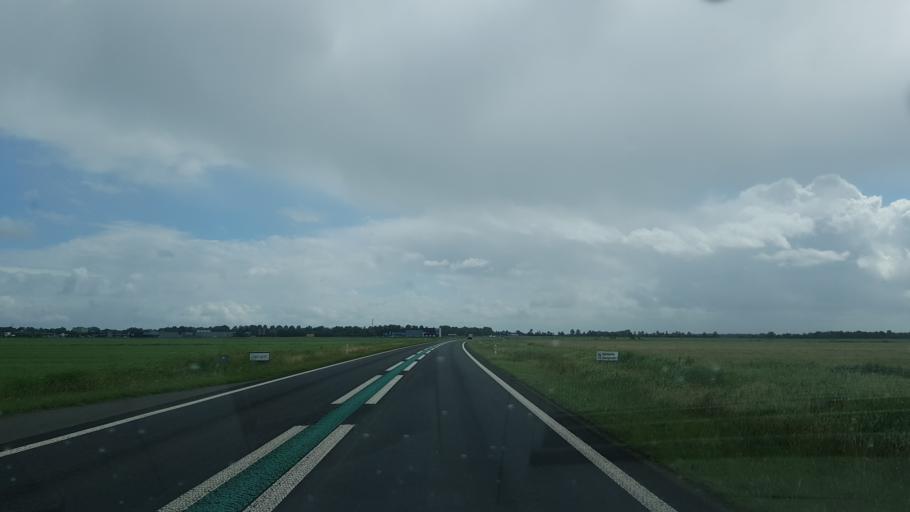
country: NL
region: Friesland
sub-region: Gemeente Dongeradeel
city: Dokkum
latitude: 53.3089
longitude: 5.9758
